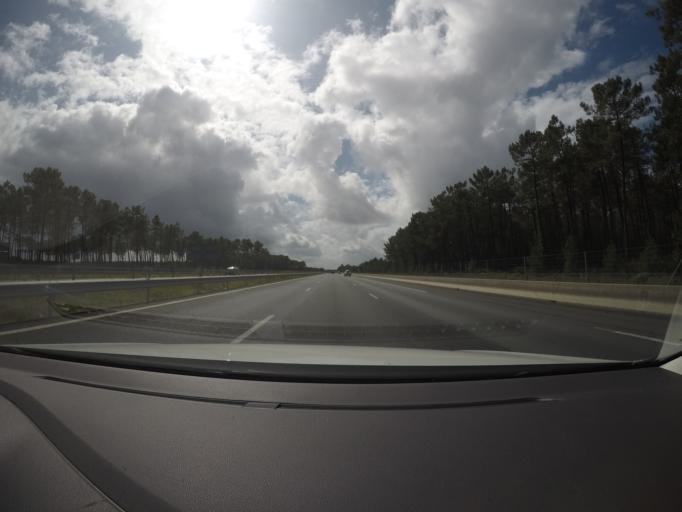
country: FR
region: Aquitaine
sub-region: Departement des Landes
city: Magescq
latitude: 43.7493
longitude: -1.2242
